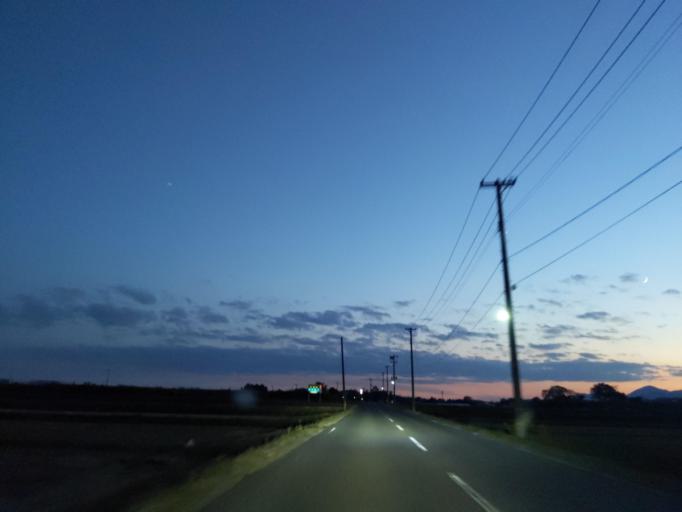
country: JP
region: Fukushima
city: Koriyama
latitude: 37.4291
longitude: 140.3140
